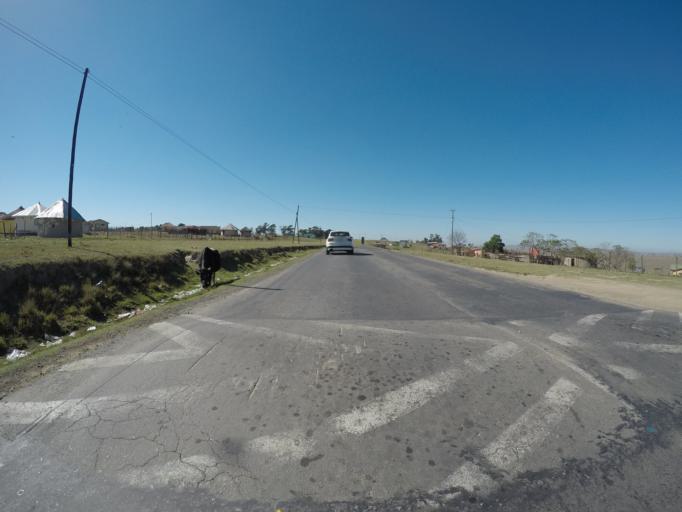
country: ZA
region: Eastern Cape
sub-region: OR Tambo District Municipality
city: Mthatha
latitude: -31.7873
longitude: 28.7428
